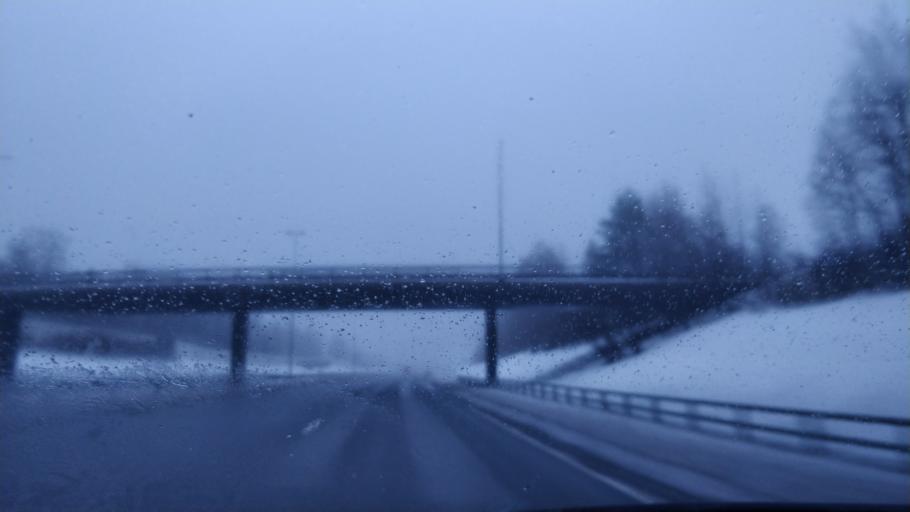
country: FI
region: Lapland
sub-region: Kemi-Tornio
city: Kemi
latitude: 65.7503
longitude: 24.5758
